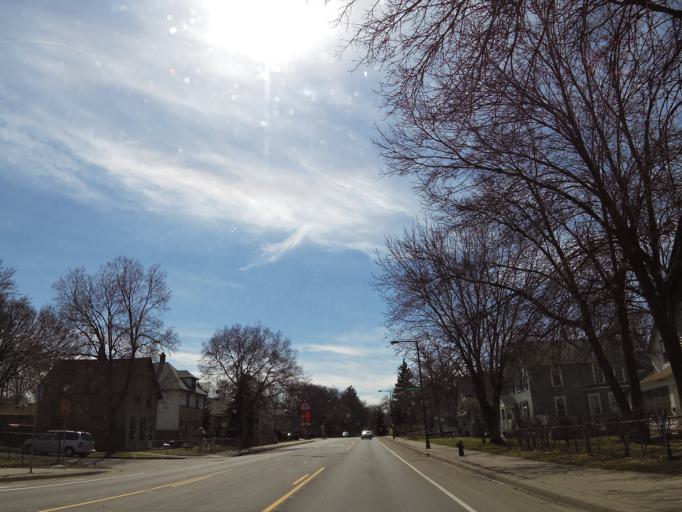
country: US
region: Minnesota
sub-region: Ramsey County
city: Maplewood
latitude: 44.9681
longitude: -93.0450
